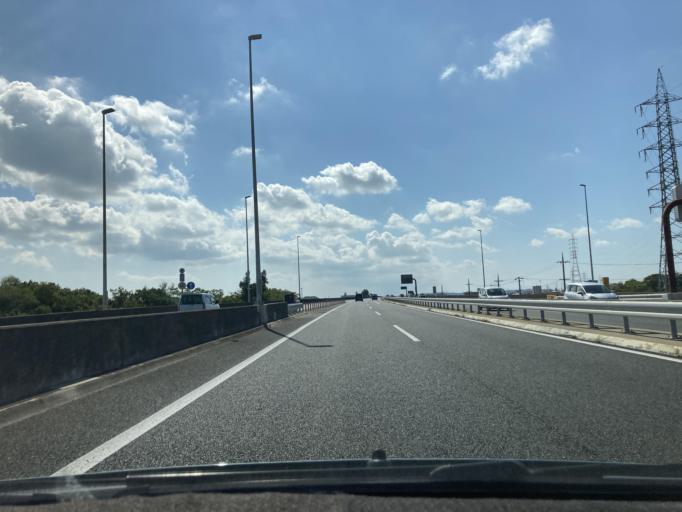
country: JP
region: Okinawa
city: Tomigusuku
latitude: 26.1953
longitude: 127.7397
